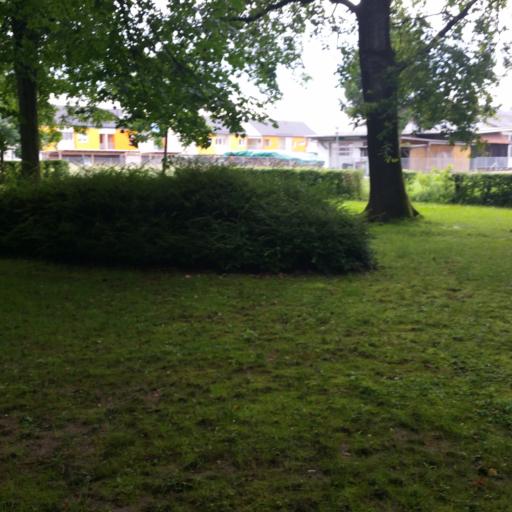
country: AT
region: Styria
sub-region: Politischer Bezirk Leibnitz
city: Gleinstatten
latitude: 46.7531
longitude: 15.3668
